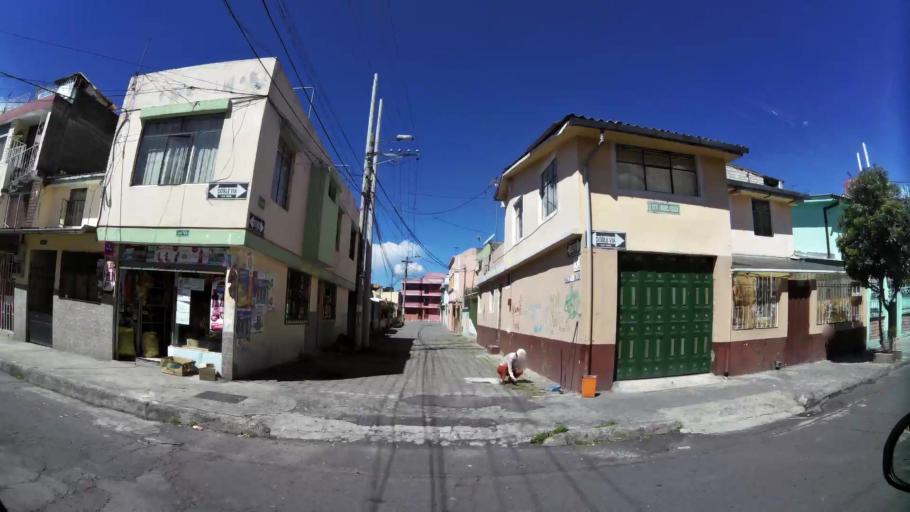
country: EC
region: Pichincha
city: Quito
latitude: -0.2557
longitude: -78.5358
